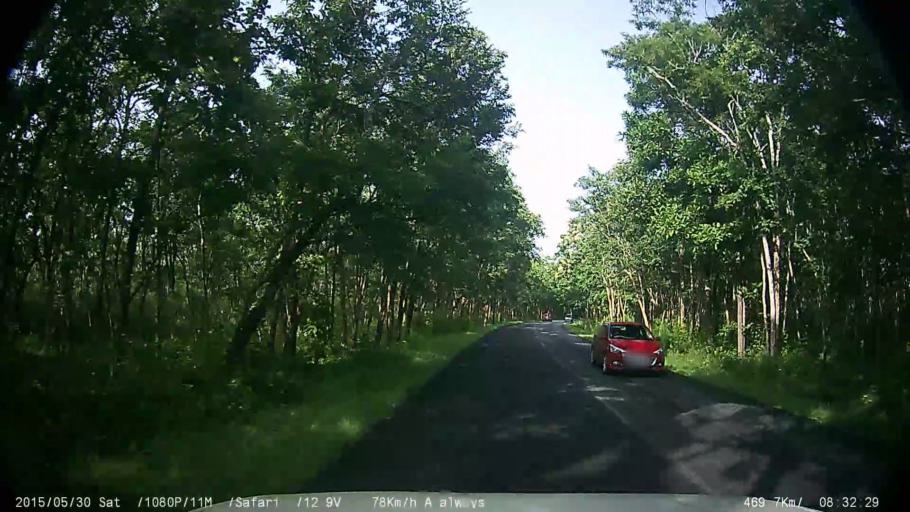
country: IN
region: Tamil Nadu
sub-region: Nilgiri
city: Masinigudi
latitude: 11.7308
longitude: 76.4537
